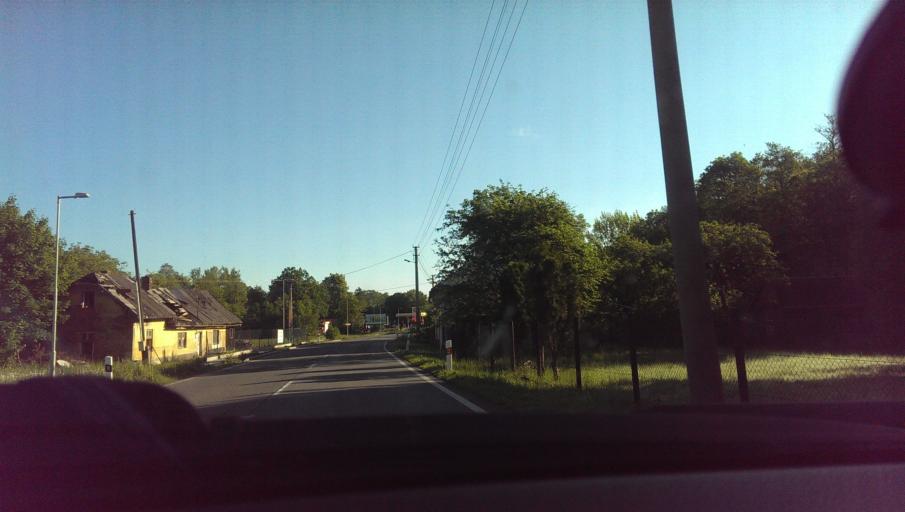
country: CZ
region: Moravskoslezsky
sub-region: Okres Frydek-Mistek
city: Celadna
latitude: 49.5561
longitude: 18.3447
